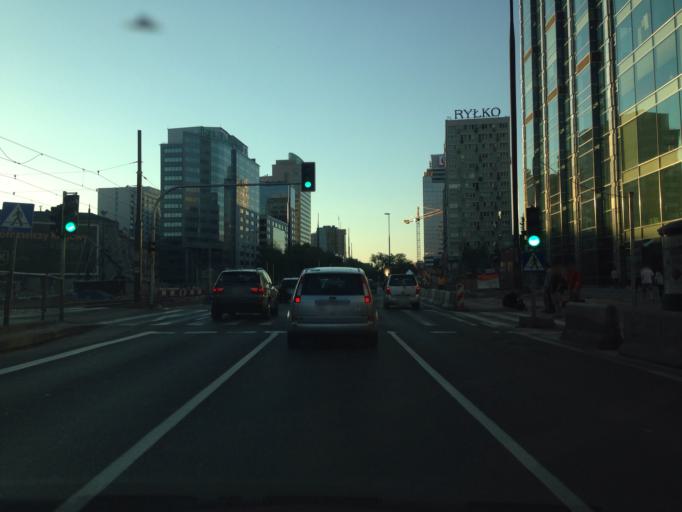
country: PL
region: Masovian Voivodeship
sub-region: Warszawa
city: Warsaw
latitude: 52.2320
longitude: 20.9993
